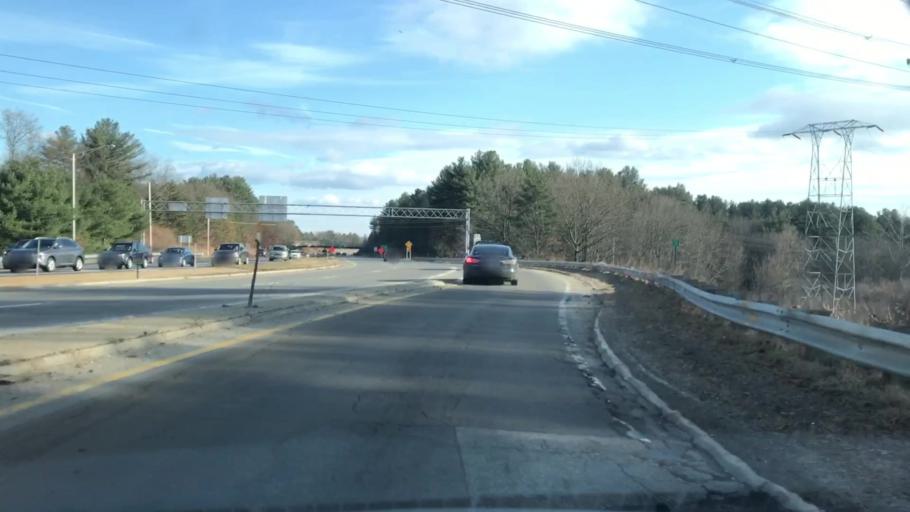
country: US
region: New Hampshire
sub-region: Hillsborough County
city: Bedford
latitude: 42.9594
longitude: -71.5016
